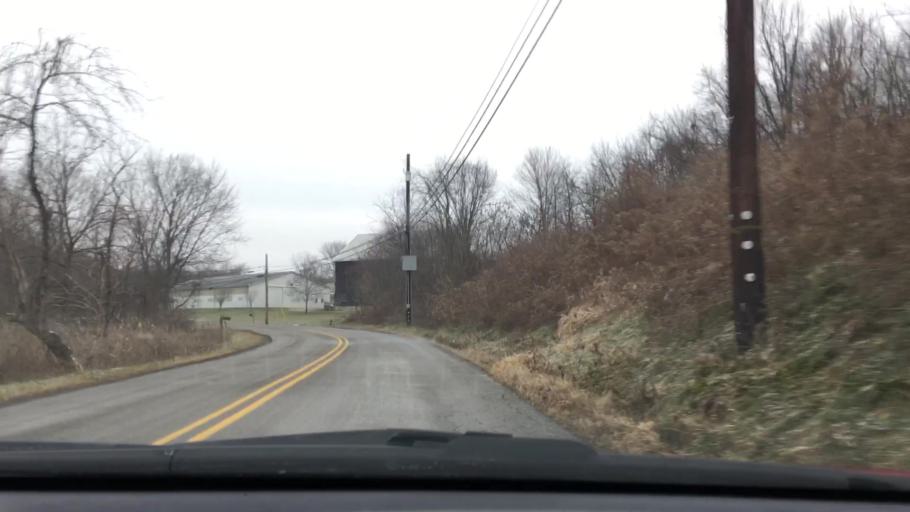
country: US
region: Pennsylvania
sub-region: Allegheny County
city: Imperial
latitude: 40.4227
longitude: -80.2346
